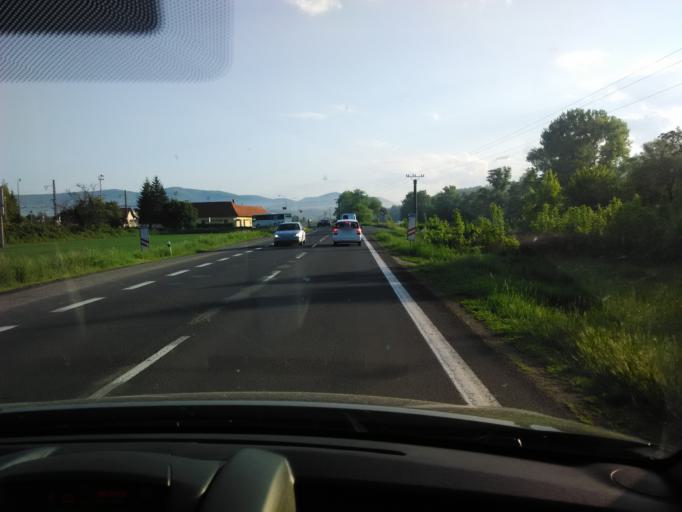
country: SK
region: Nitriansky
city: Tlmace
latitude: 48.3084
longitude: 18.5356
